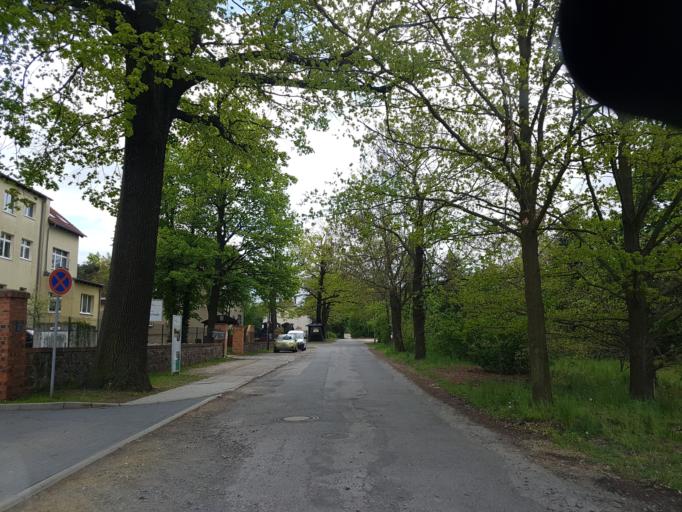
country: DE
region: Brandenburg
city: Altdobern
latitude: 51.6492
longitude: 14.0395
